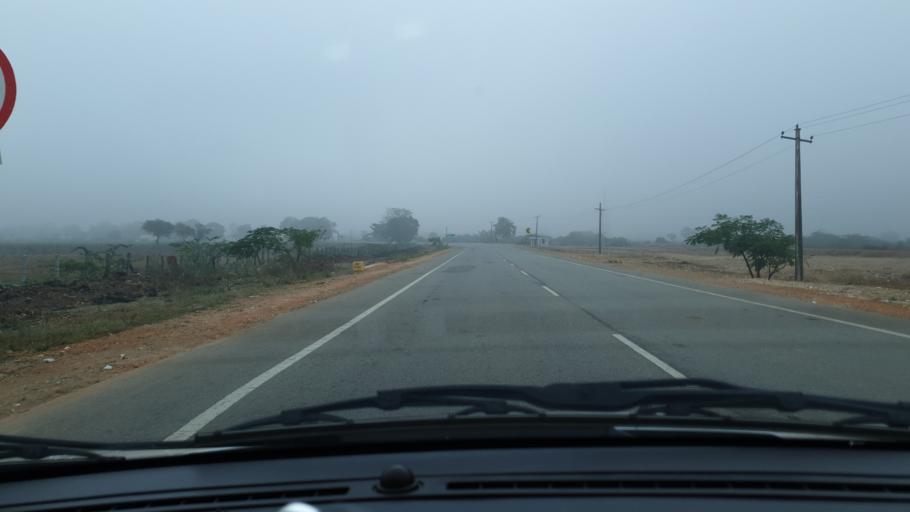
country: IN
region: Telangana
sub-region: Nalgonda
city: Devarkonda
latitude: 16.6315
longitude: 78.6081
